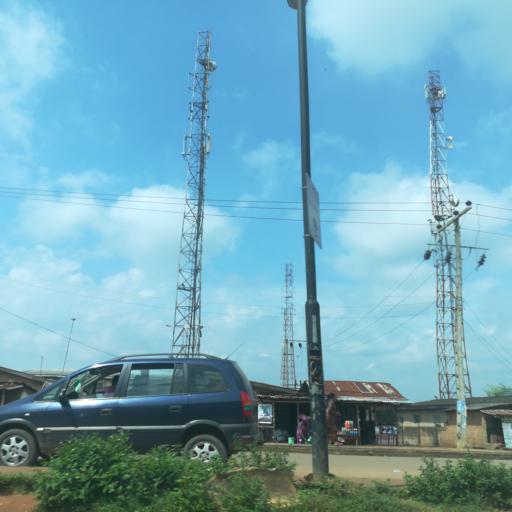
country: NG
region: Lagos
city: Ikorodu
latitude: 6.6686
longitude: 3.6726
